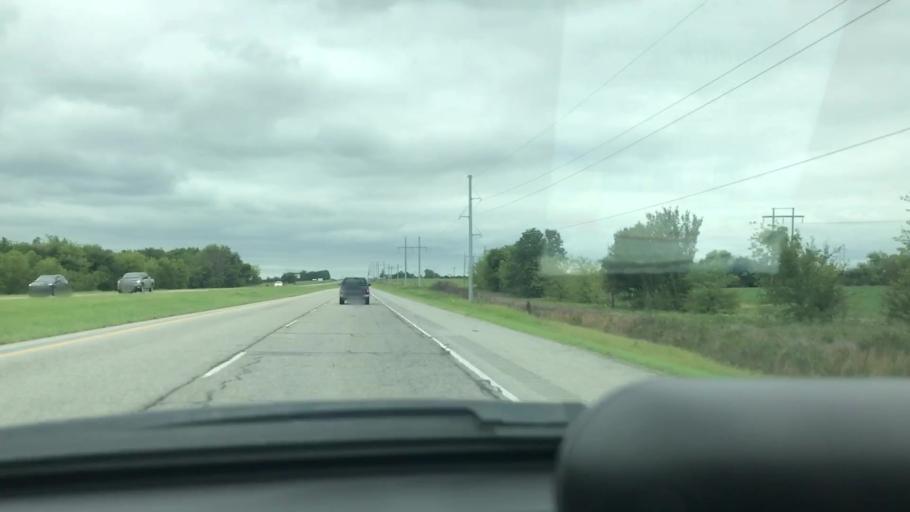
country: US
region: Oklahoma
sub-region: Wagoner County
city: Wagoner
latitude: 36.0038
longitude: -95.3686
